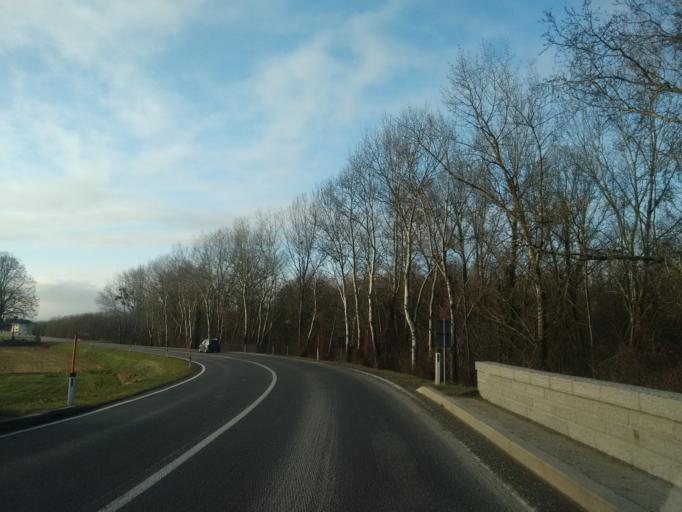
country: AT
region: Lower Austria
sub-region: Politischer Bezirk Melk
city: Melk
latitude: 48.2179
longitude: 15.3120
